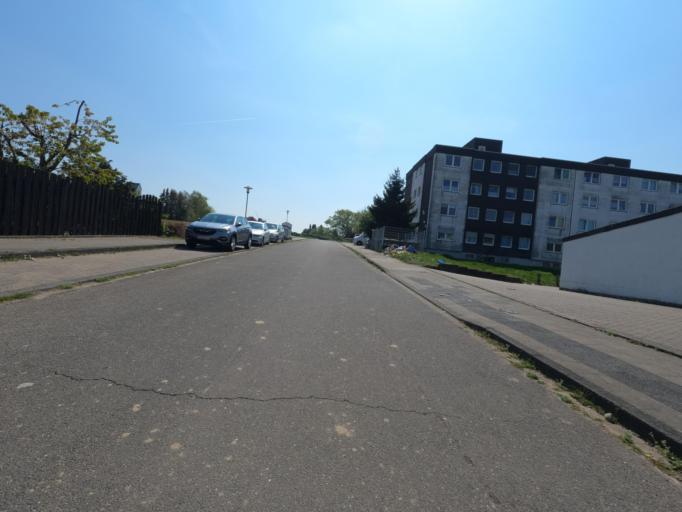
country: DE
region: North Rhine-Westphalia
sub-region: Regierungsbezirk Koln
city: Ubach-Palenberg
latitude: 50.9091
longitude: 6.1352
